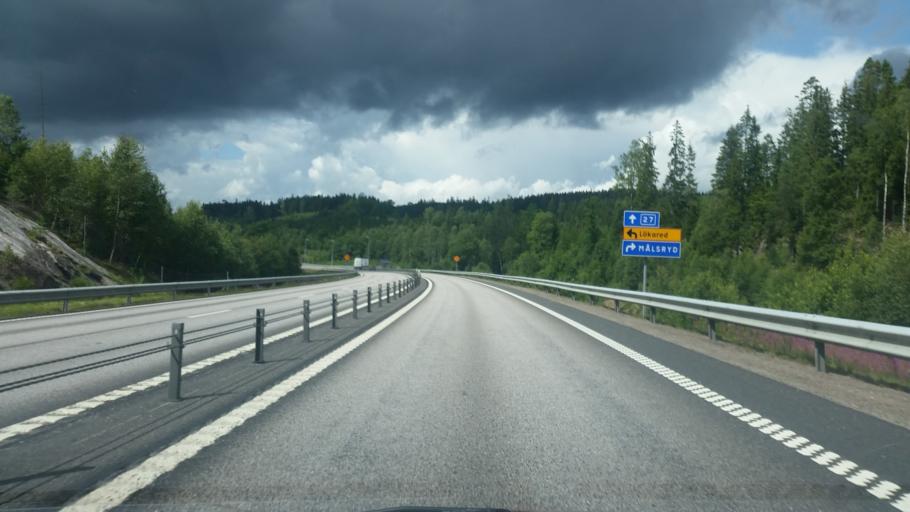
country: SE
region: Vaestra Goetaland
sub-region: Boras Kommun
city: Ganghester
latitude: 57.6700
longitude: 13.0262
